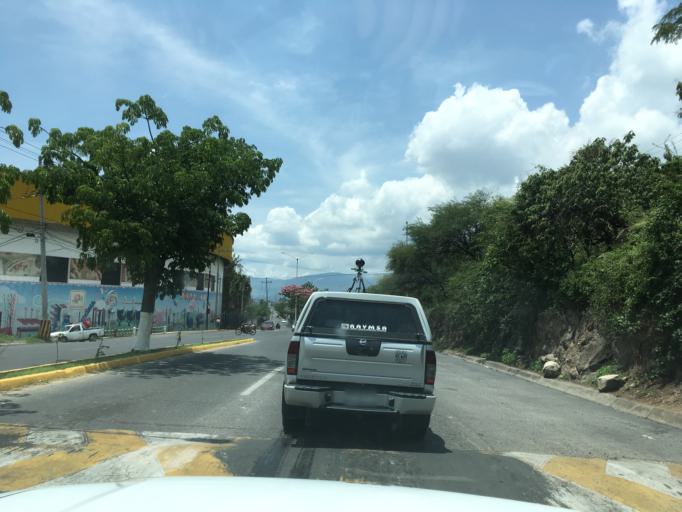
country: MX
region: Jalisco
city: Tlajomulco de Zuniga
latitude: 20.4654
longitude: -103.4486
